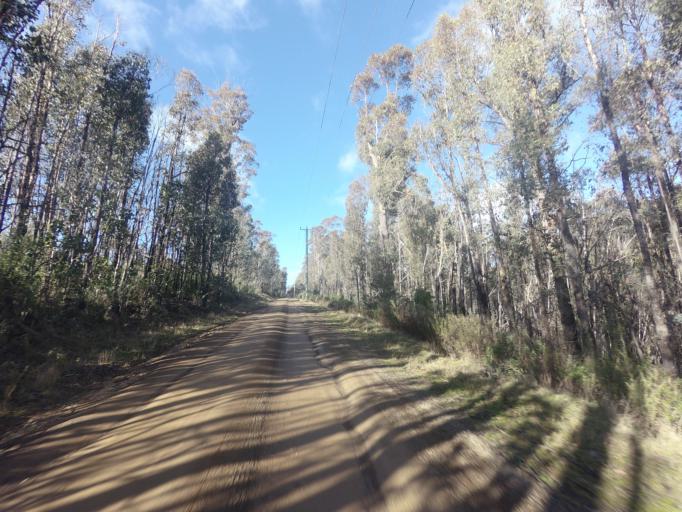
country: AU
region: Tasmania
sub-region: Derwent Valley
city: New Norfolk
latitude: -42.8421
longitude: 147.1388
